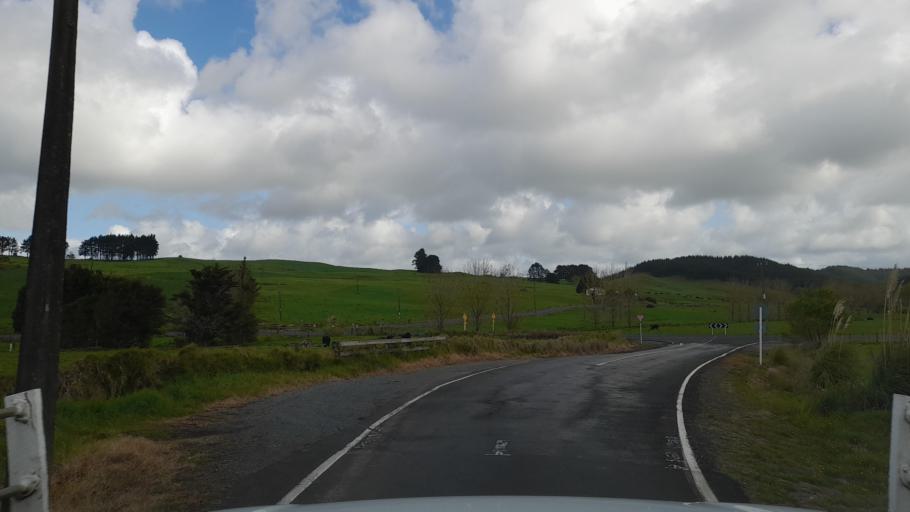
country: NZ
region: Northland
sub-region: Whangarei
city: Maungatapere
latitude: -35.7730
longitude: 174.2459
